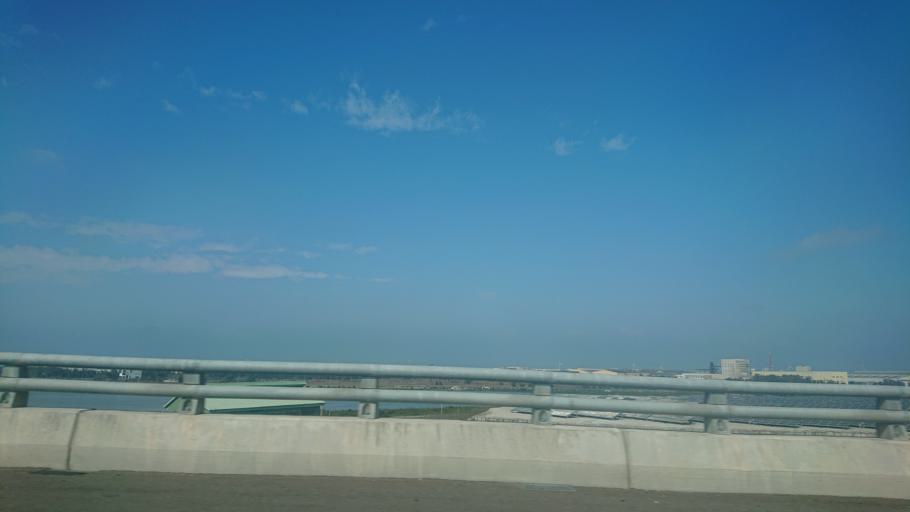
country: TW
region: Taiwan
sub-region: Changhua
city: Chang-hua
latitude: 24.0583
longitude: 120.4091
